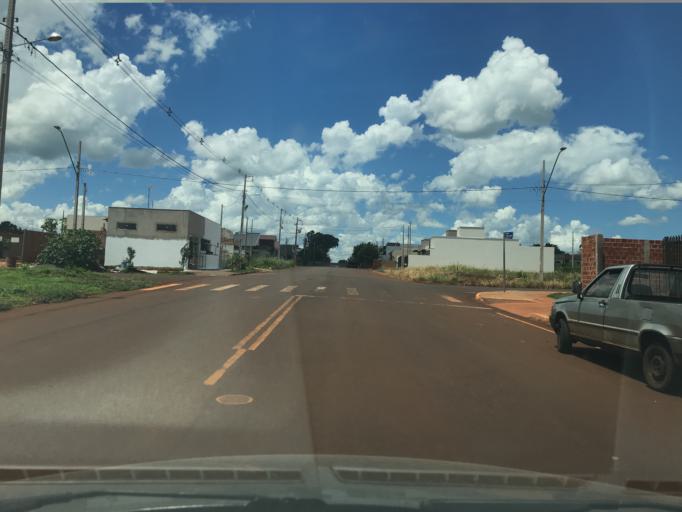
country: BR
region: Parana
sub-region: Palotina
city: Palotina
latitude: -24.2648
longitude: -53.8454
